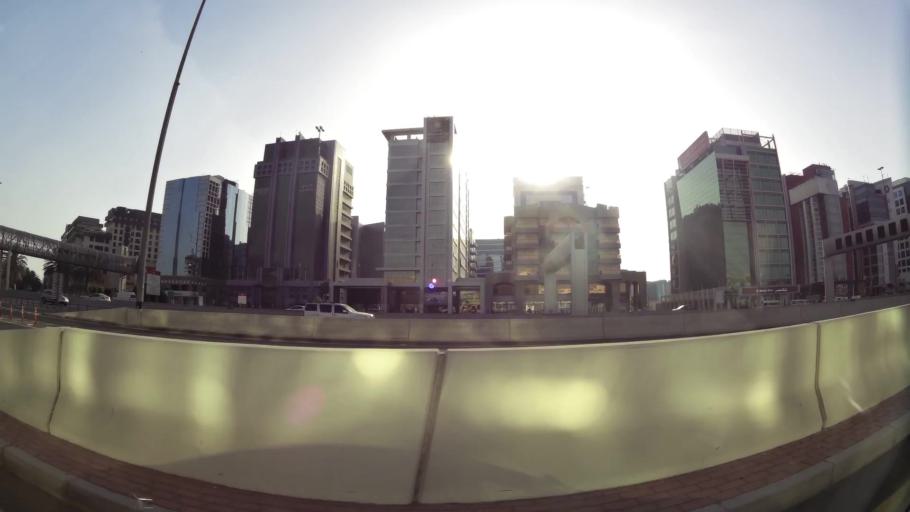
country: AE
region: Ash Shariqah
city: Sharjah
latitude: 25.2528
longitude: 55.3367
